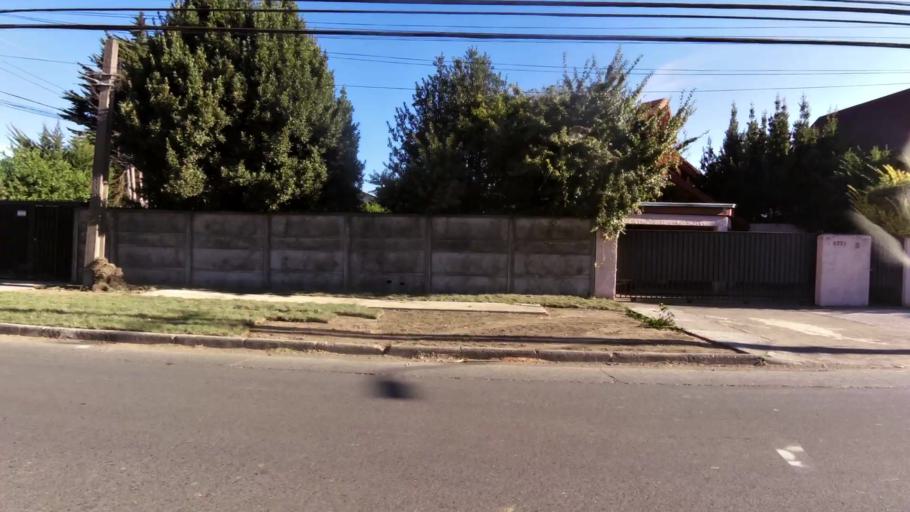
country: CL
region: Biobio
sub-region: Provincia de Concepcion
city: Concepcion
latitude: -36.8344
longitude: -73.1099
